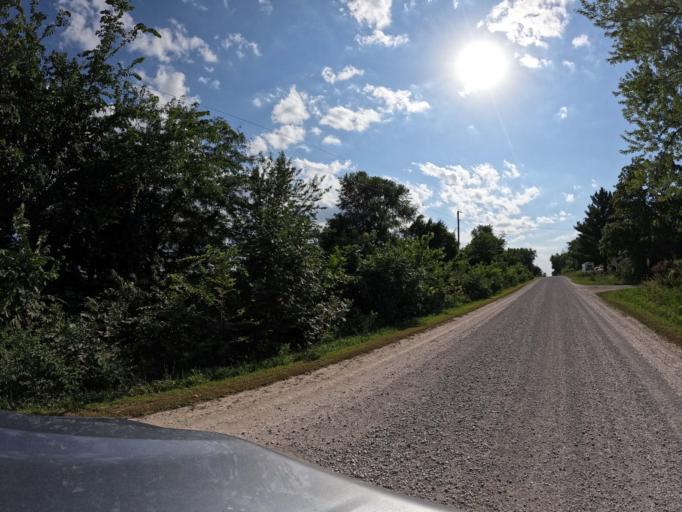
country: US
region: Iowa
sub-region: Appanoose County
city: Centerville
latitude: 40.7179
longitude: -93.0268
